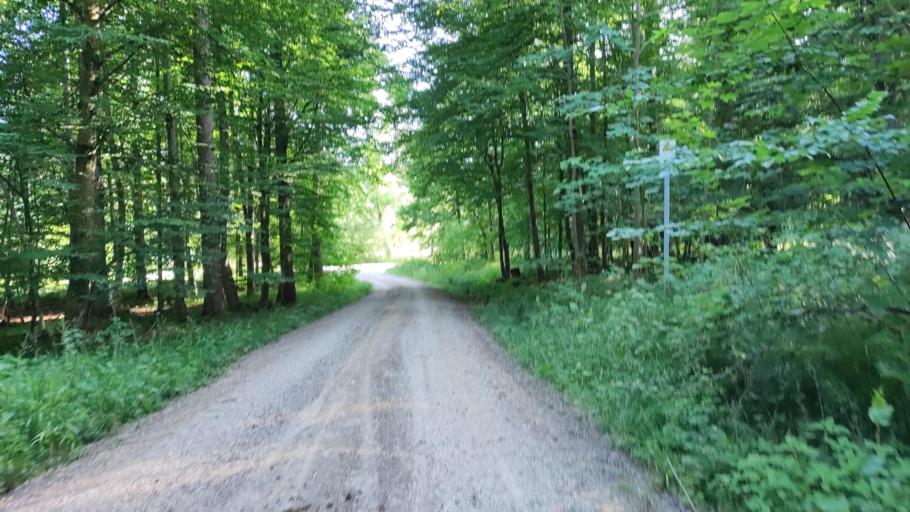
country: DE
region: Bavaria
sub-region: Swabia
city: Rosshaupten
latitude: 48.4165
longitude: 10.4940
